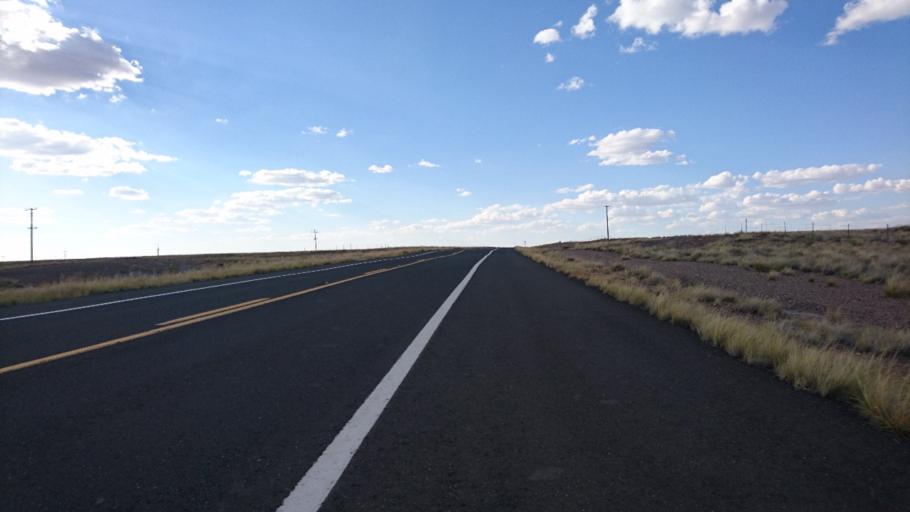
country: US
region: Arizona
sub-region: Navajo County
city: Holbrook
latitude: 34.7940
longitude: -109.8990
